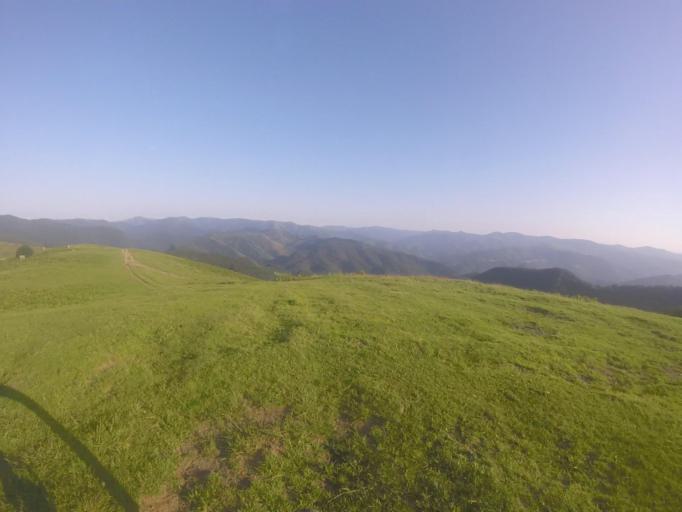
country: ES
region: Navarre
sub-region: Provincia de Navarra
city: Arano
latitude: 43.2442
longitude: -1.8492
